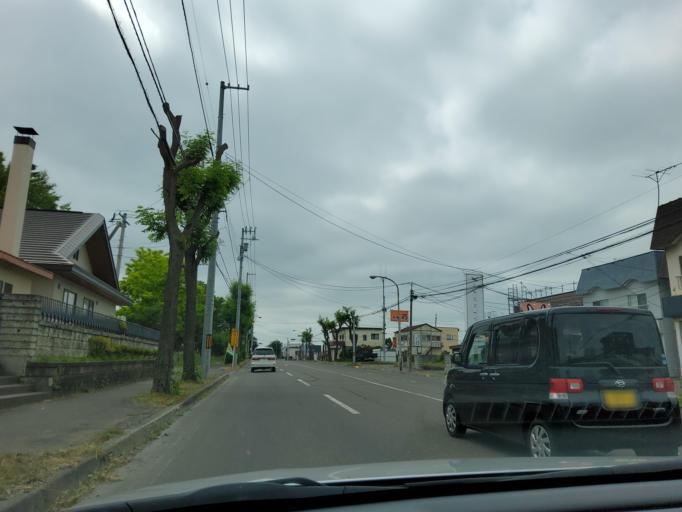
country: JP
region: Hokkaido
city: Obihiro
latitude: 42.9147
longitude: 143.1741
